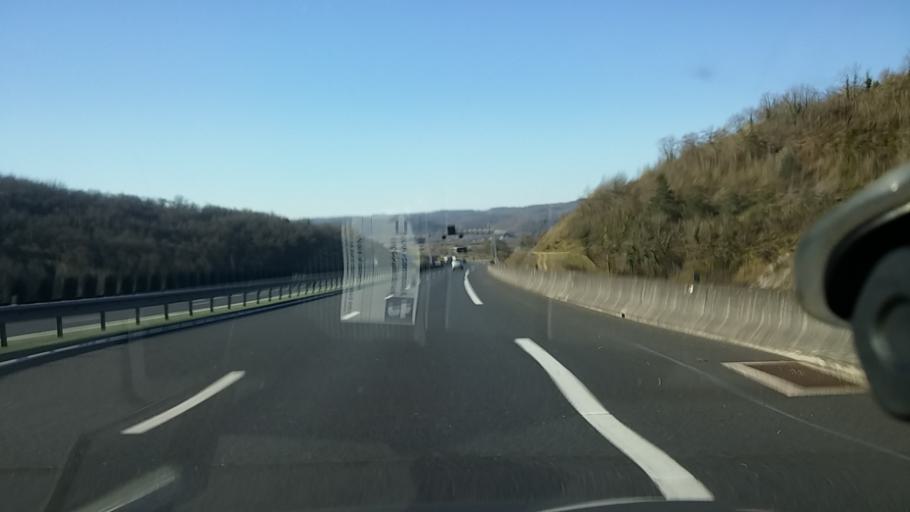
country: FR
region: Midi-Pyrenees
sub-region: Departement du Lot
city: Souillac
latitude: 44.8692
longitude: 1.5056
